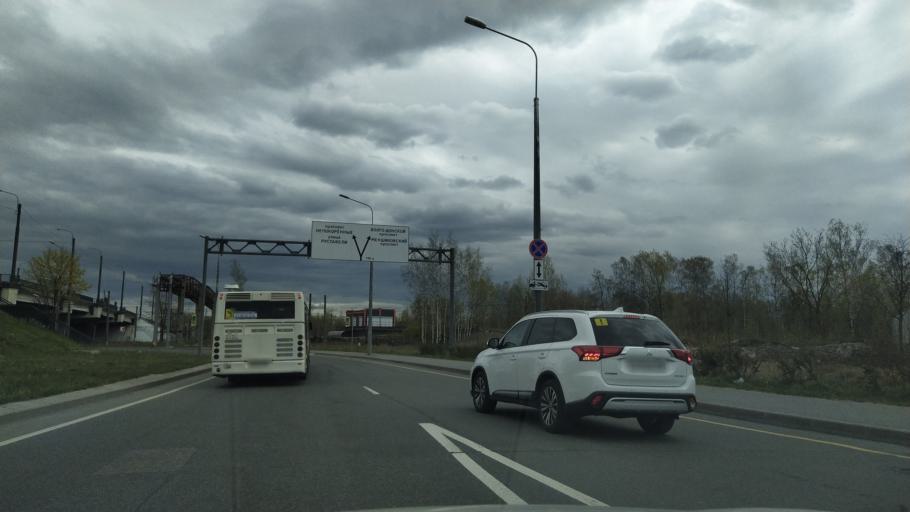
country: RU
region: St.-Petersburg
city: Krasnogvargeisky
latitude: 59.9902
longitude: 30.4404
